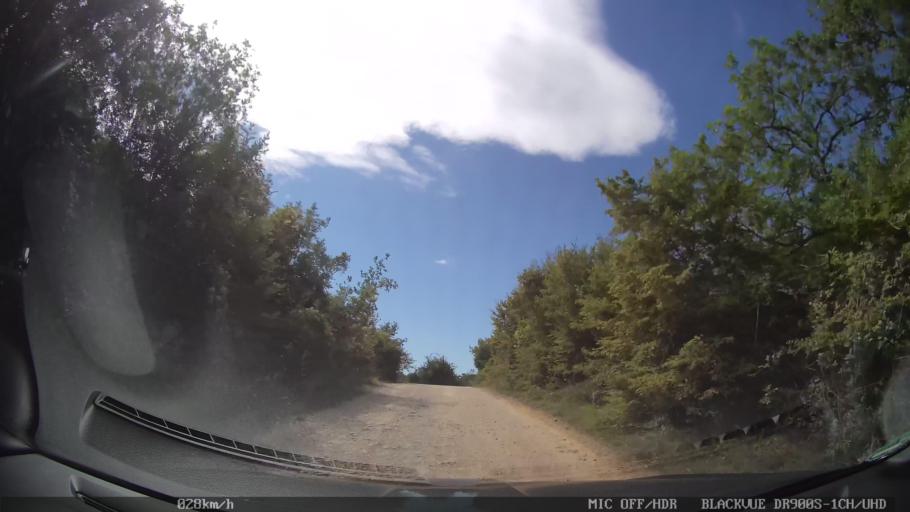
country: HR
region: Primorsko-Goranska
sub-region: Grad Krk
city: Krk
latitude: 45.0449
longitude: 14.5307
